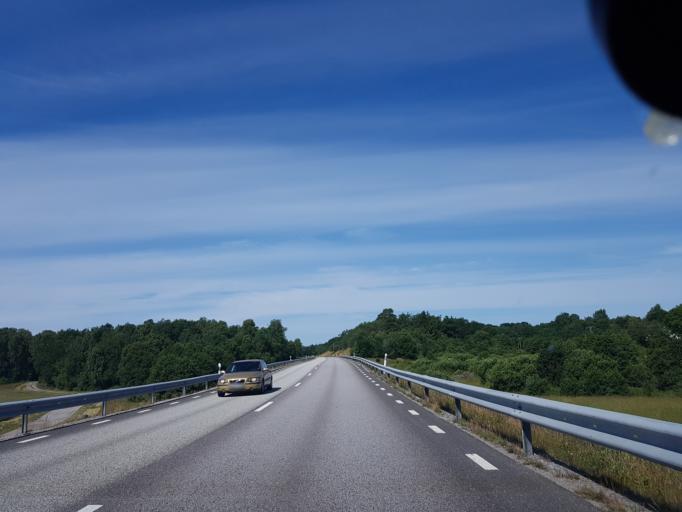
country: SE
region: Vaestra Goetaland
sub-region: Orust
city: Henan
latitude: 58.1548
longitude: 11.5588
